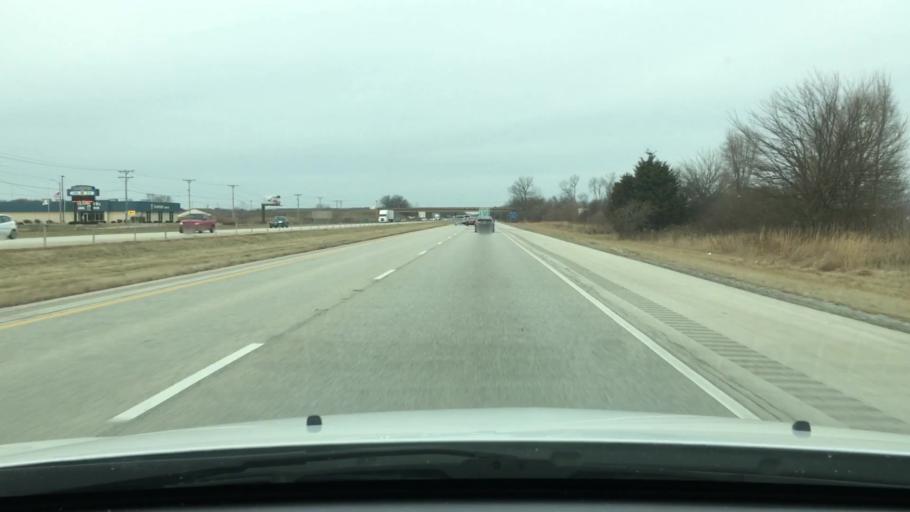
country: US
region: Illinois
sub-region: Sangamon County
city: Grandview
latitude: 39.8415
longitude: -89.5938
